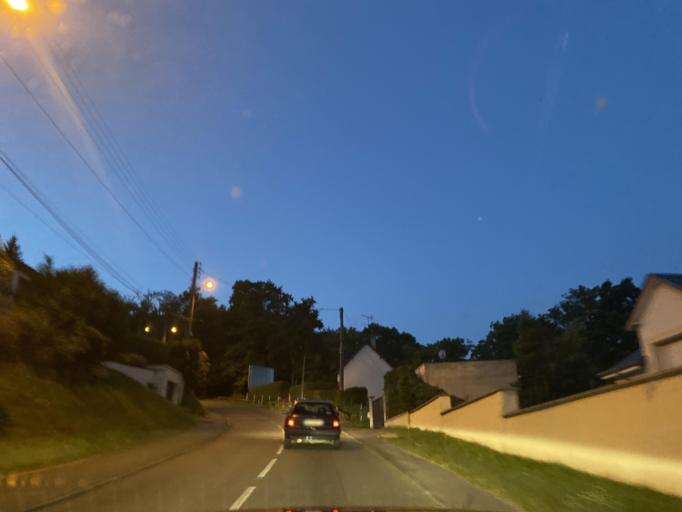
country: FR
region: Haute-Normandie
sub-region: Departement de l'Eure
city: Evreux
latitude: 49.0278
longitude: 1.1673
